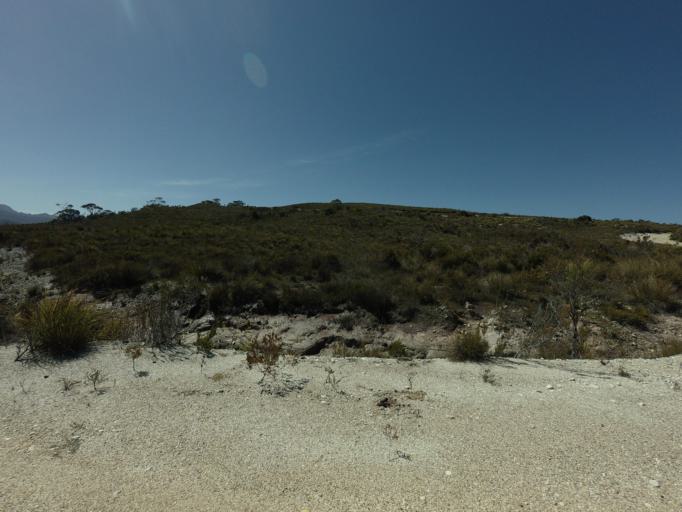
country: AU
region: Tasmania
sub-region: Huon Valley
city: Geeveston
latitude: -43.0323
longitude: 146.3328
